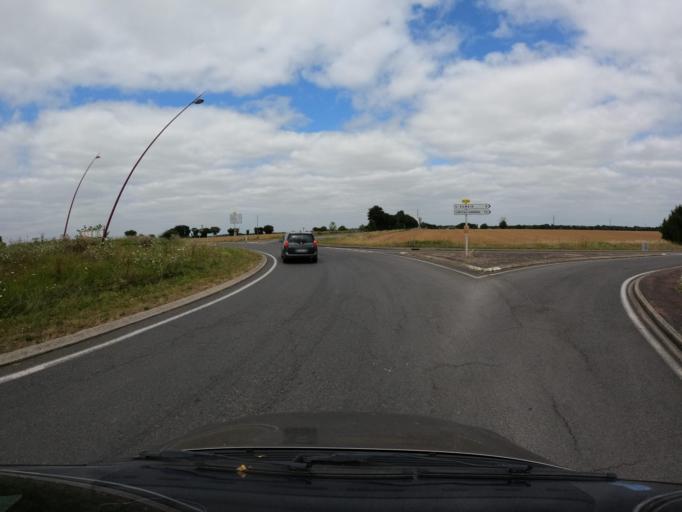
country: FR
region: Poitou-Charentes
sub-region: Departement de la Vienne
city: Civray
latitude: 46.1626
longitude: 0.2994
